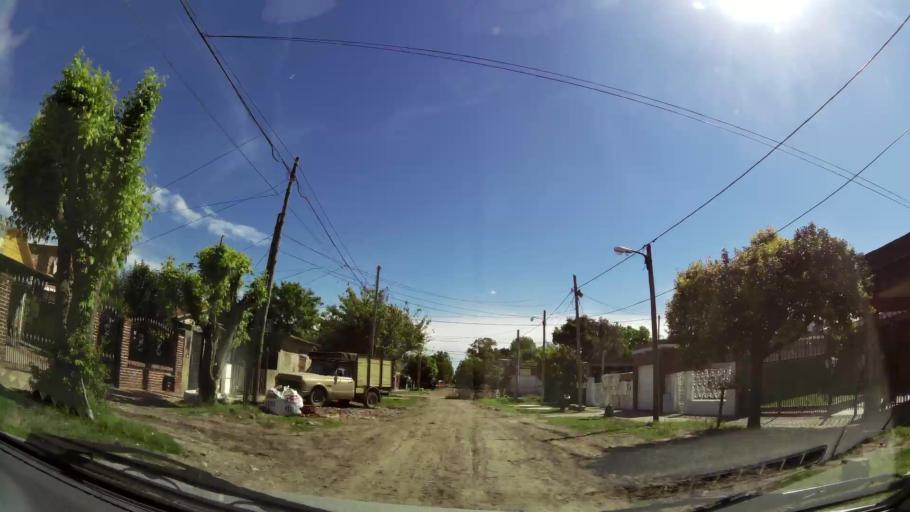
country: AR
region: Buenos Aires
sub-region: Partido de Almirante Brown
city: Adrogue
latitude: -34.7794
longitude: -58.3492
